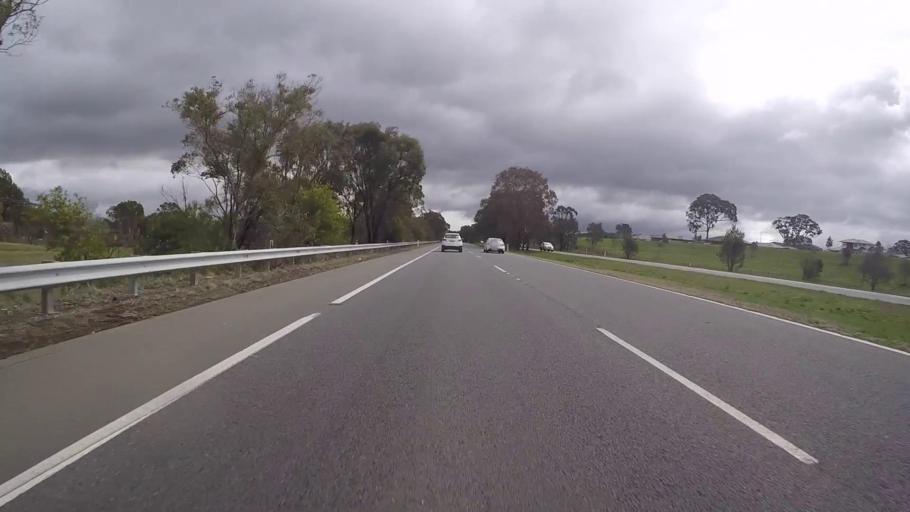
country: AU
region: Australian Capital Territory
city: Kaleen
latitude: -35.2090
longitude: 149.1071
